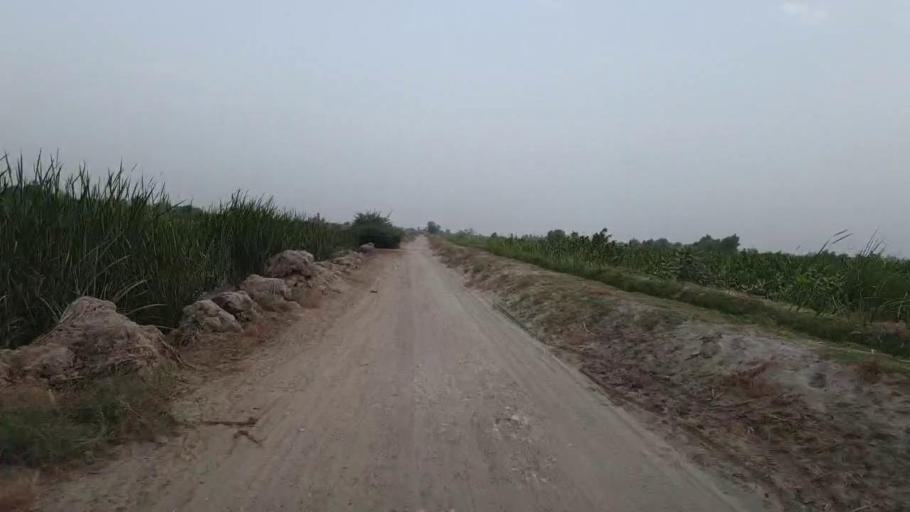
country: PK
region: Sindh
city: Daur
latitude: 26.4140
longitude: 68.2251
